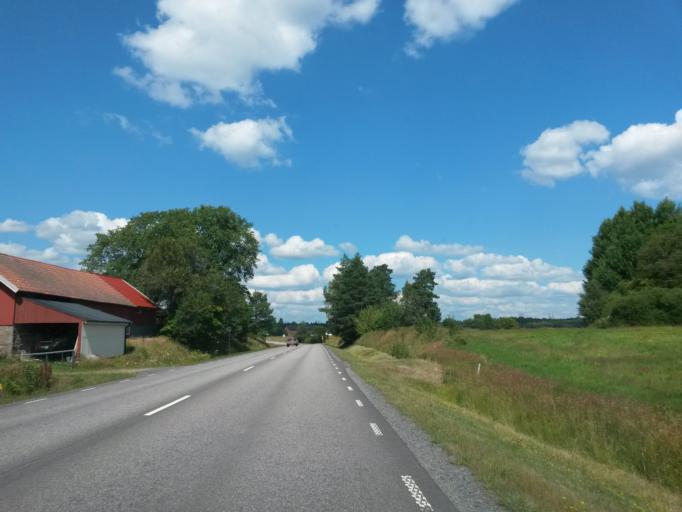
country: SE
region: Vaestra Goetaland
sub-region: Lerums Kommun
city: Stenkullen
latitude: 57.8133
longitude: 12.3018
